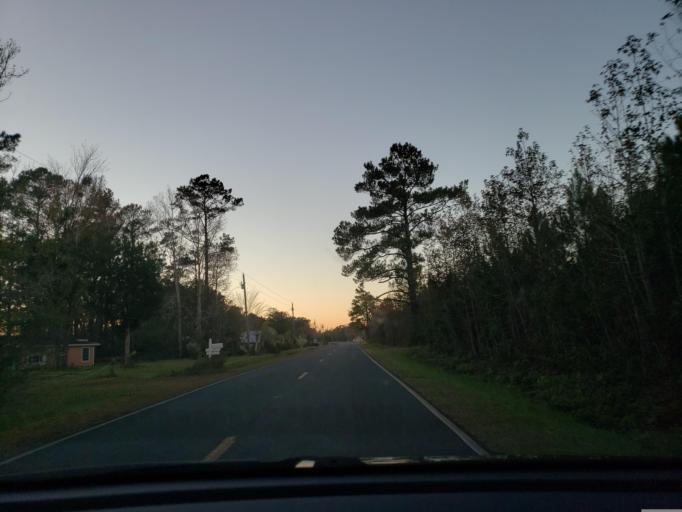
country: US
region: North Carolina
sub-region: Onslow County
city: Richlands
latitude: 34.7423
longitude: -77.6381
